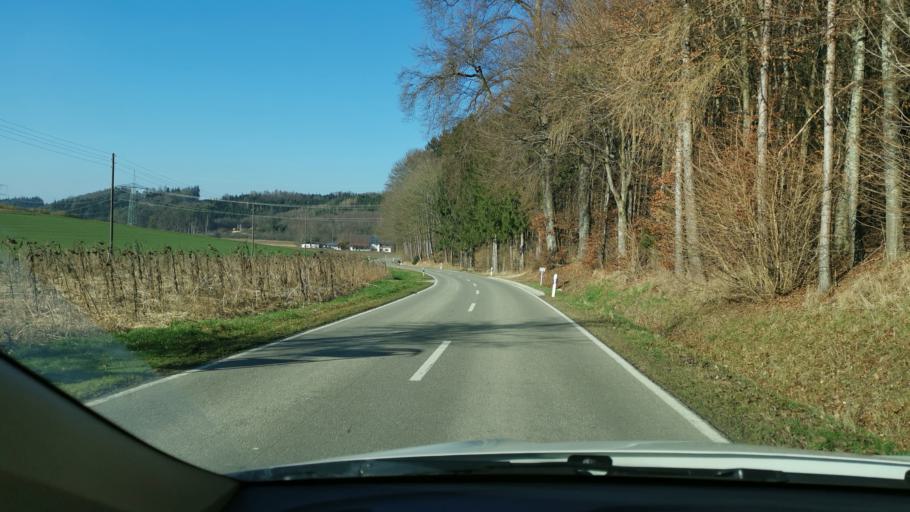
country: DE
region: Bavaria
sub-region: Swabia
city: Rehling
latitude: 48.4911
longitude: 10.9465
